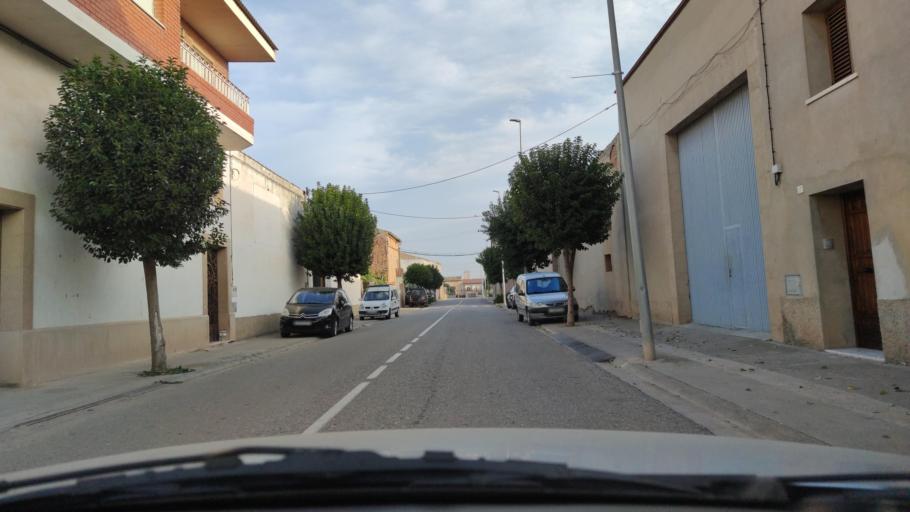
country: ES
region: Catalonia
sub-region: Provincia de Lleida
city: Anglesola
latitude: 41.6533
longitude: 1.0813
